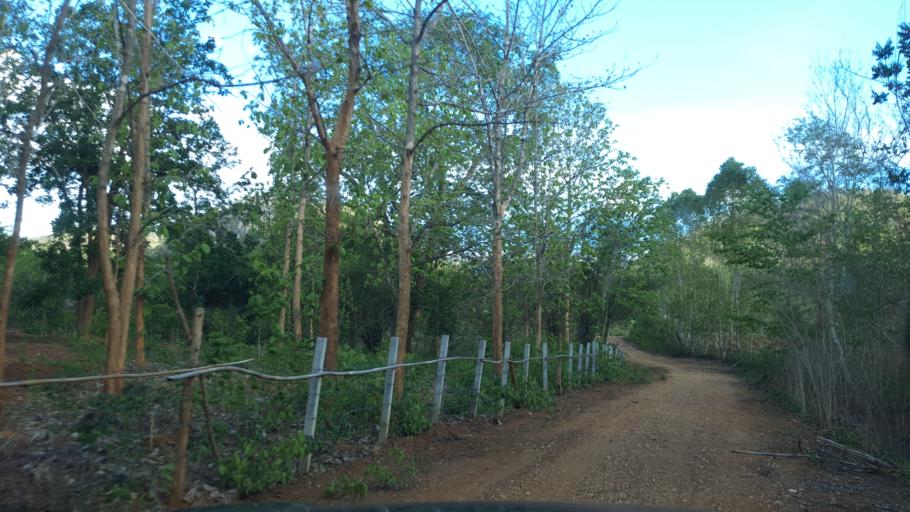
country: TH
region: Lampang
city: Sop Prap
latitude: 17.8498
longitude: 99.2847
